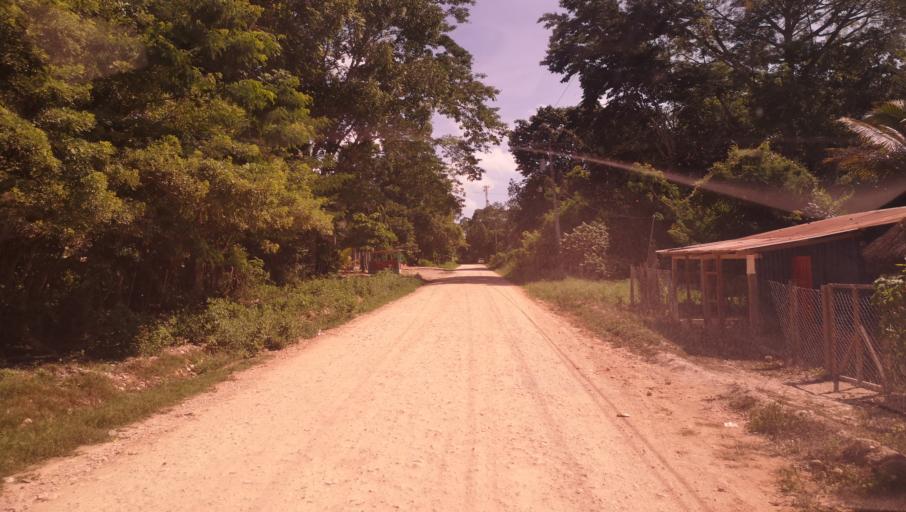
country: GT
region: Peten
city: Melchor de Mencos
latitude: 16.8391
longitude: -89.2994
